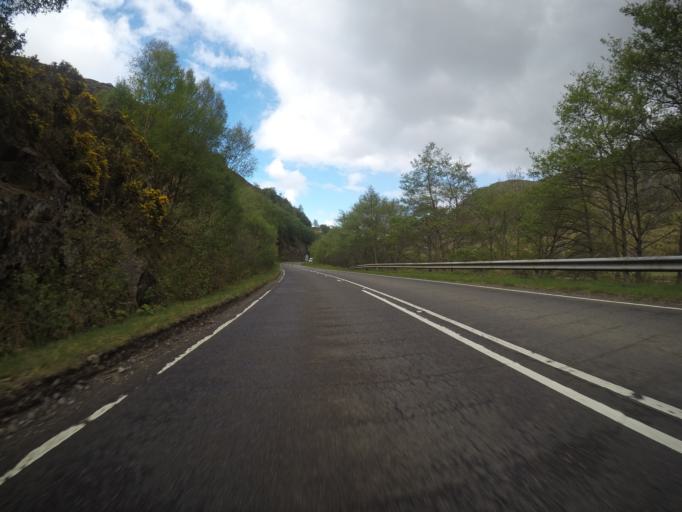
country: GB
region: Scotland
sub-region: Highland
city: Fort William
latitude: 57.2084
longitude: -5.4061
